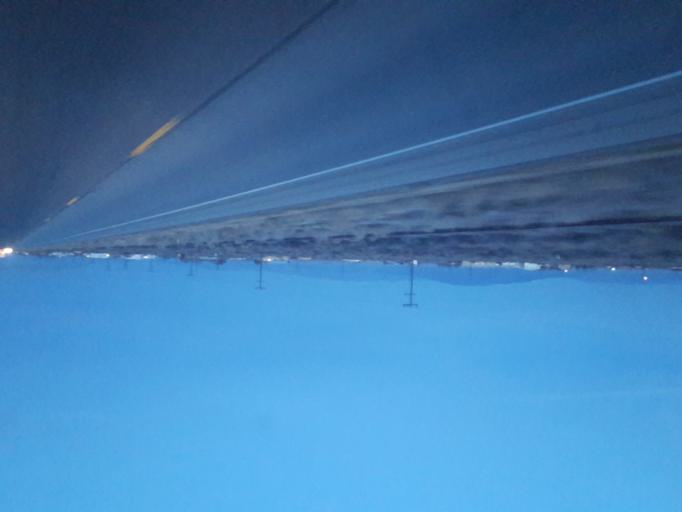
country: US
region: Colorado
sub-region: Alamosa County
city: Alamosa
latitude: 37.4865
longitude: -105.9213
